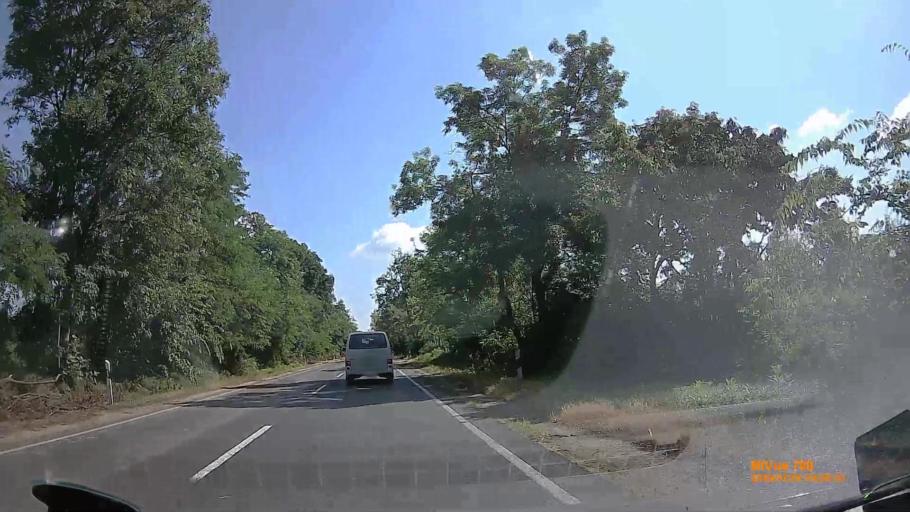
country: HU
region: Szabolcs-Szatmar-Bereg
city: Nyirmada
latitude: 48.0621
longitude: 22.2180
